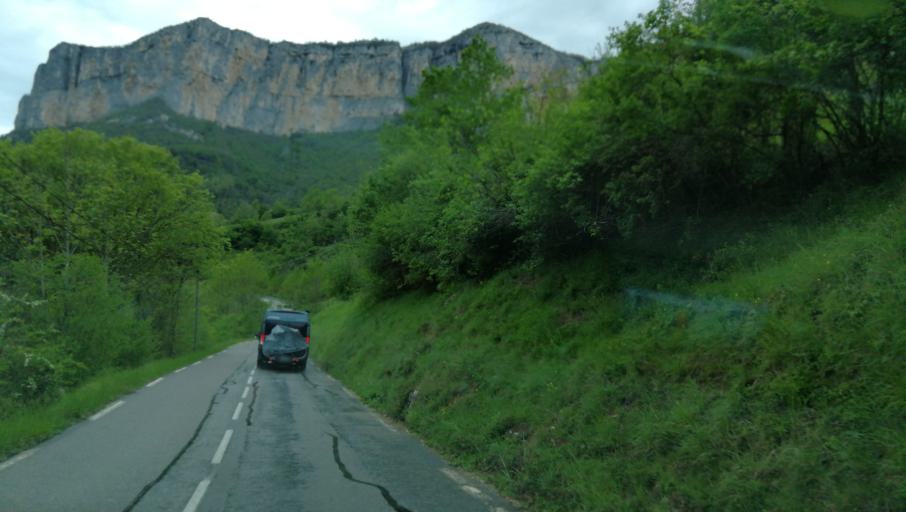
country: FR
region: Rhone-Alpes
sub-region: Departement de l'Isere
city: Pont-en-Royans
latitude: 45.0634
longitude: 5.3996
